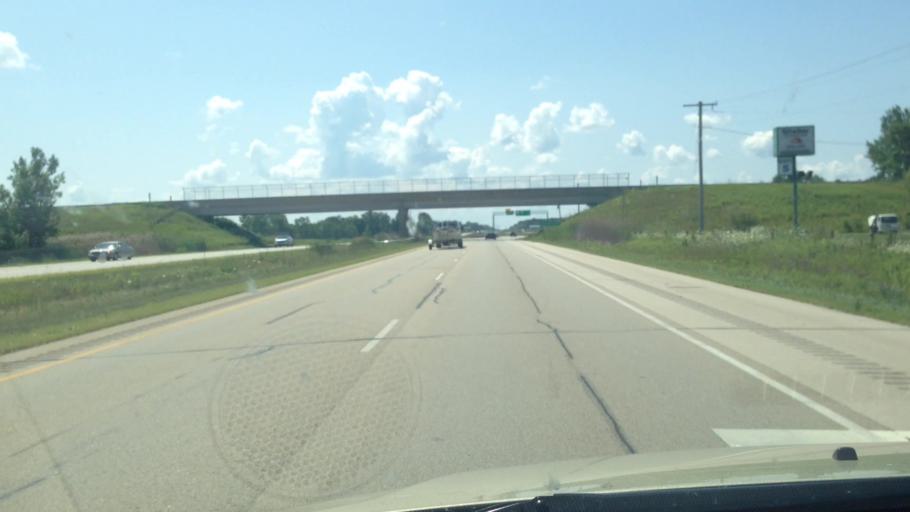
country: US
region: Wisconsin
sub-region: Brown County
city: Suamico
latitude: 44.7517
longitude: -88.0511
